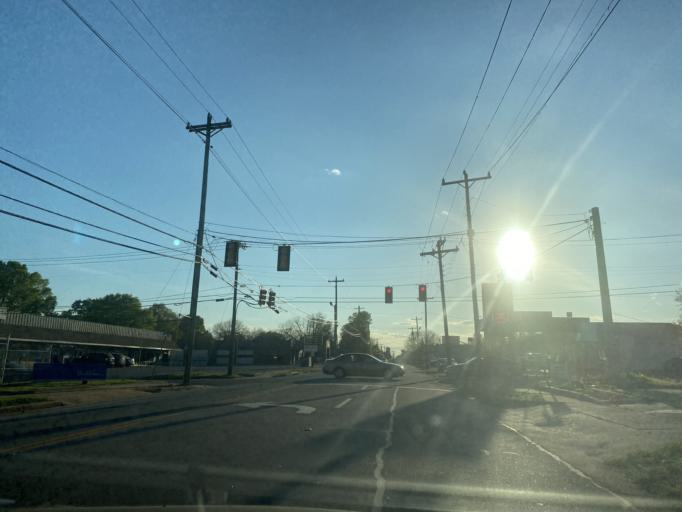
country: US
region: South Carolina
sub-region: Cherokee County
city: East Gaffney
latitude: 35.0802
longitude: -81.6328
